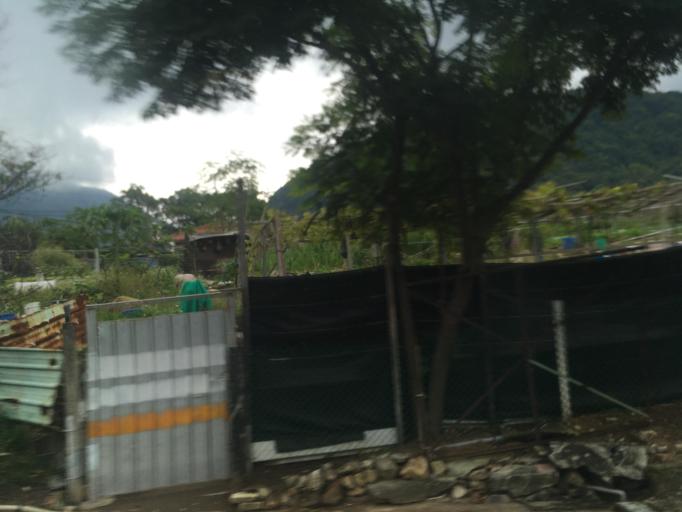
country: TW
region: Taipei
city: Taipei
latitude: 25.1359
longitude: 121.5288
